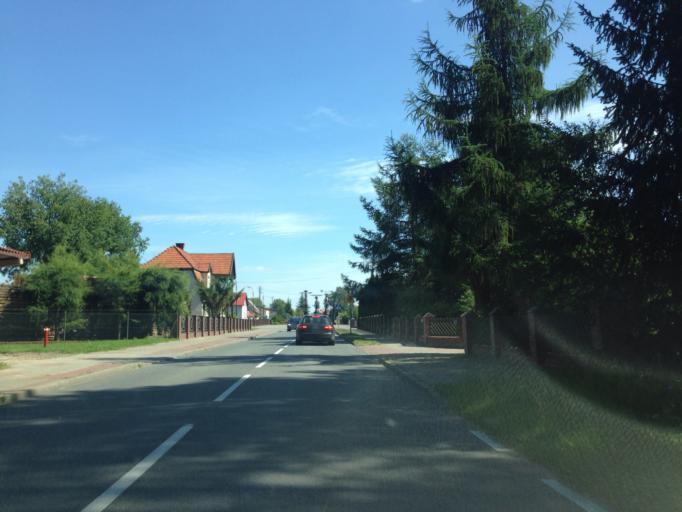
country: PL
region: Kujawsko-Pomorskie
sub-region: Powiat swiecki
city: Osie
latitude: 53.6042
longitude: 18.3327
